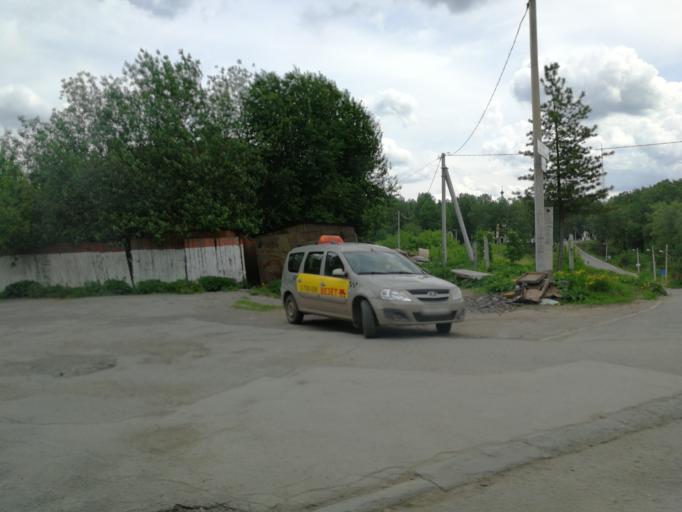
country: RU
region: Perm
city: Perm
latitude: 58.0149
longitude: 56.2642
